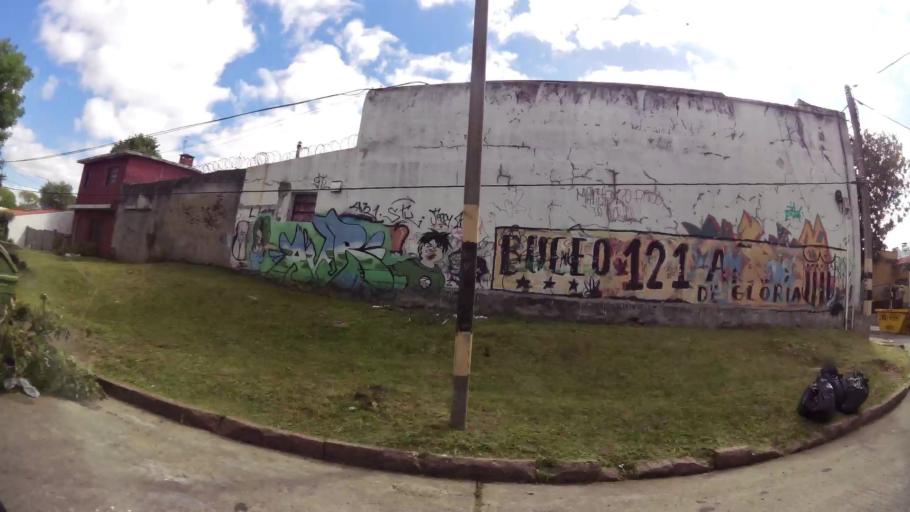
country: UY
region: Montevideo
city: Montevideo
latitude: -34.8896
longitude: -56.1305
